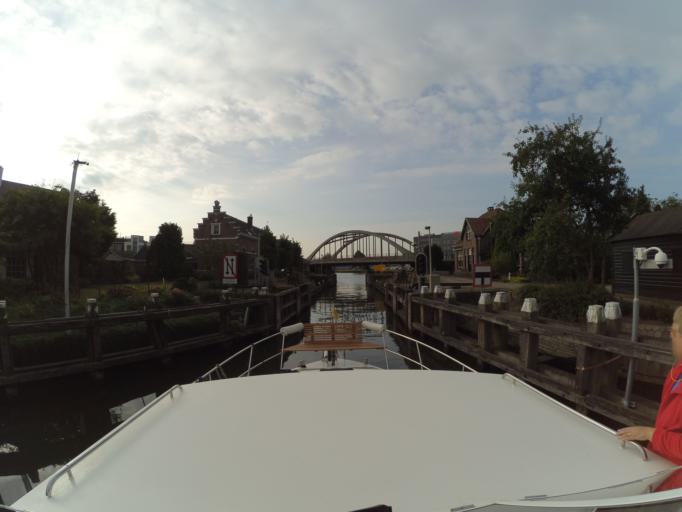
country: NL
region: Utrecht
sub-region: Stichtse Vecht
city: Maarssen
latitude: 52.1279
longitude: 5.0540
